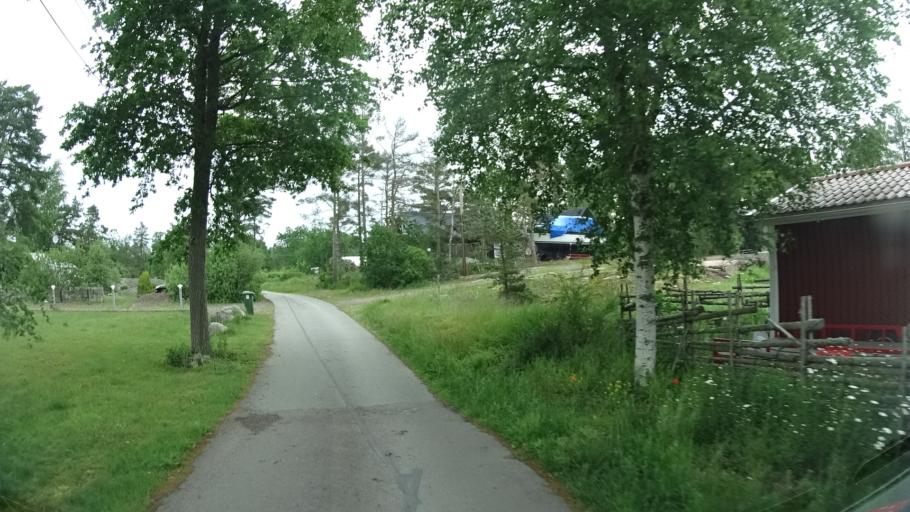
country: SE
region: Kalmar
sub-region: Oskarshamns Kommun
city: Oskarshamn
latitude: 57.2336
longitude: 16.4958
